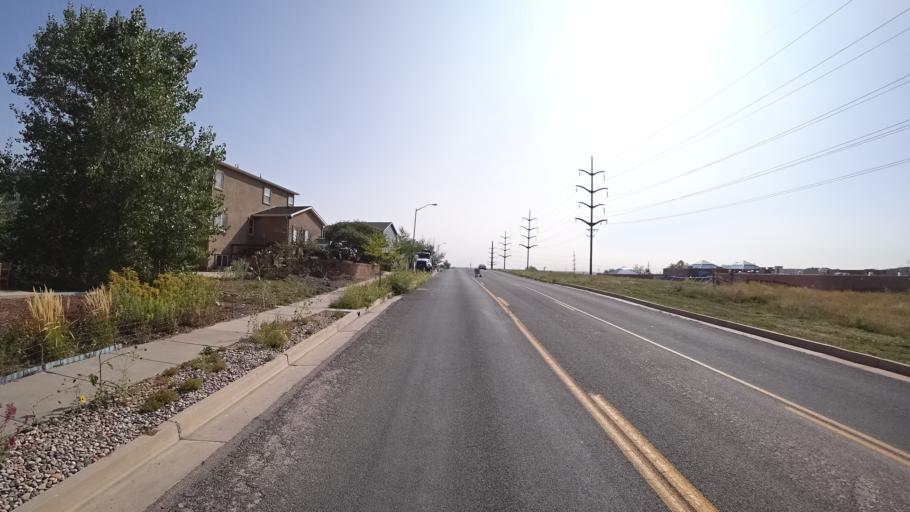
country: US
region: Colorado
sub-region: El Paso County
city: Colorado Springs
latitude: 38.8248
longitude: -104.8538
